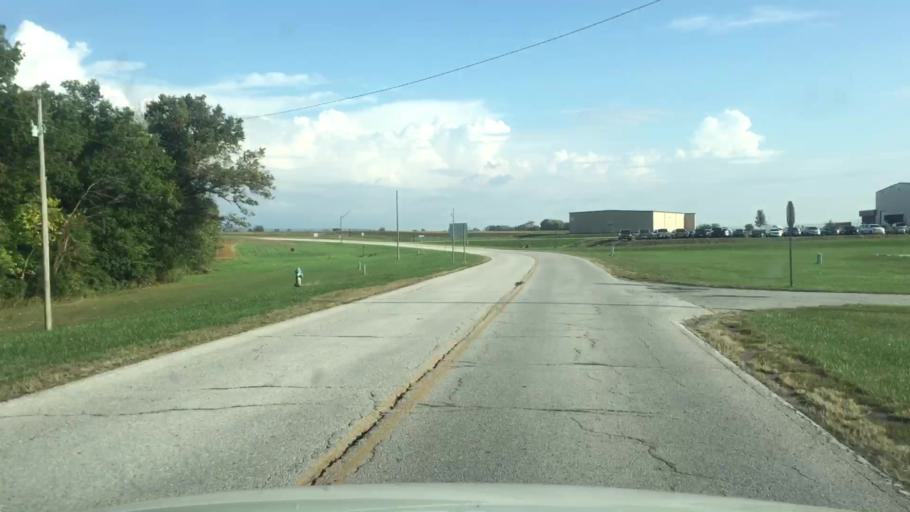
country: US
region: Missouri
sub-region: Boone County
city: Ashland
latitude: 38.8195
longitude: -92.2221
